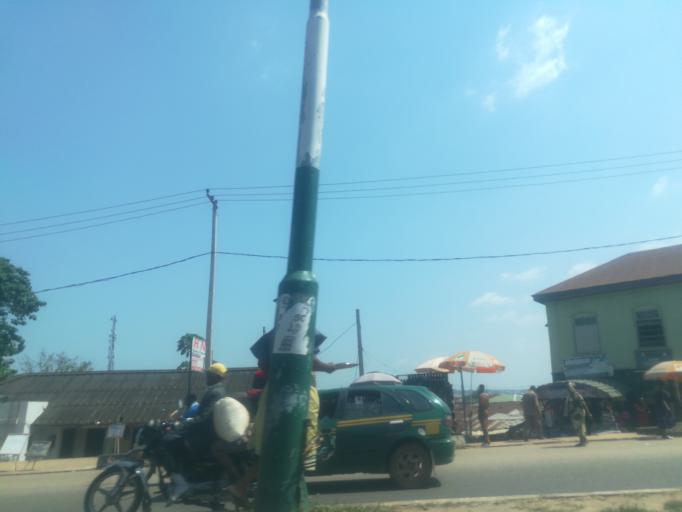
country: NG
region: Ogun
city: Abeokuta
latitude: 7.1533
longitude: 3.3459
